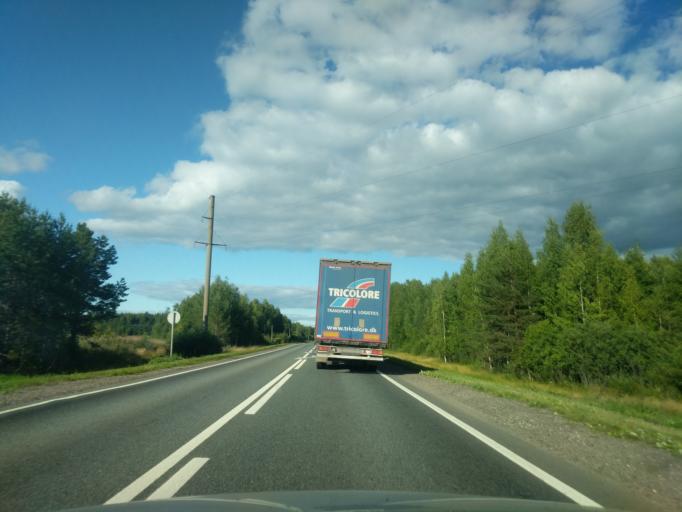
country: RU
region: Kostroma
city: Manturovo
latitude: 58.1468
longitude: 44.3669
